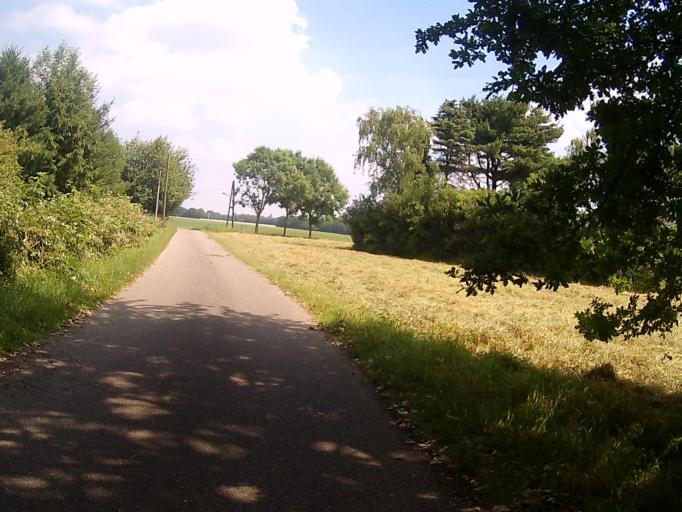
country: DE
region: North Rhine-Westphalia
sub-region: Regierungsbezirk Dusseldorf
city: Krefeld
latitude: 51.4041
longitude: 6.5672
